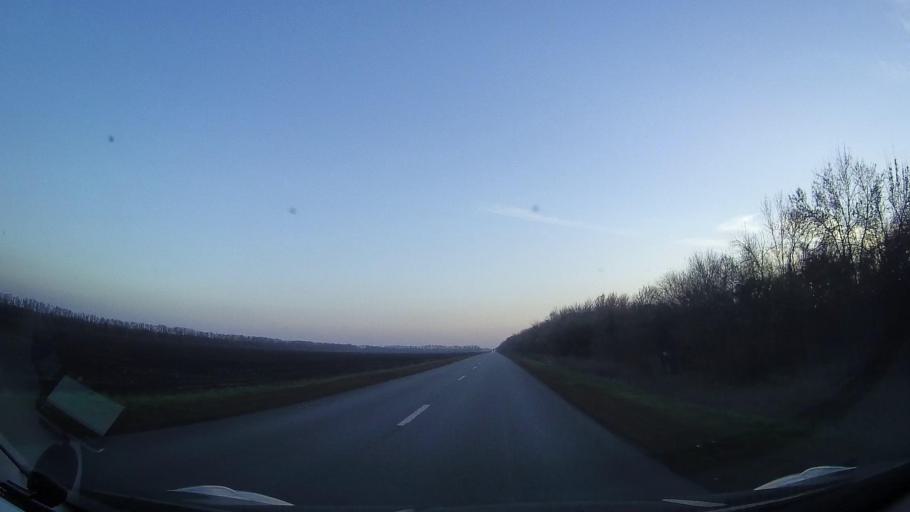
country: RU
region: Rostov
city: Zernograd
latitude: 47.0226
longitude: 40.3917
